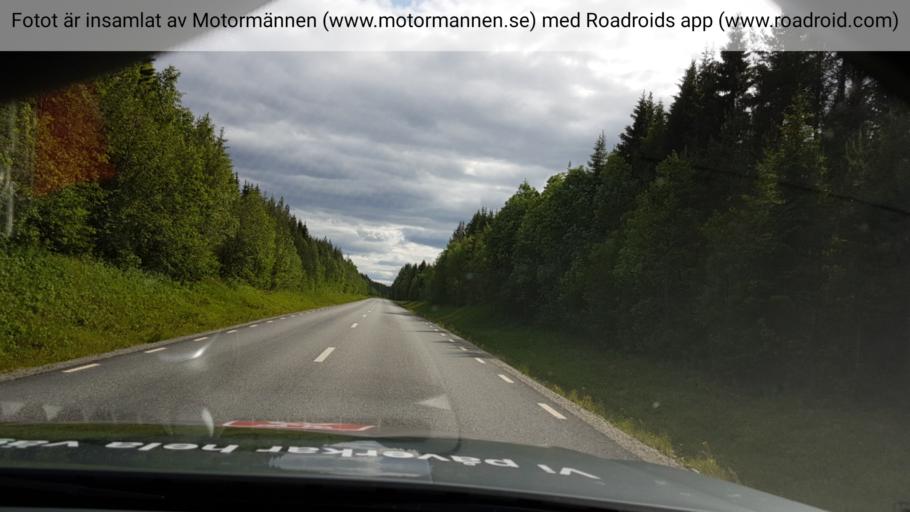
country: SE
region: Jaemtland
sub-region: Stroemsunds Kommun
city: Stroemsund
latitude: 64.0222
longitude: 15.5269
